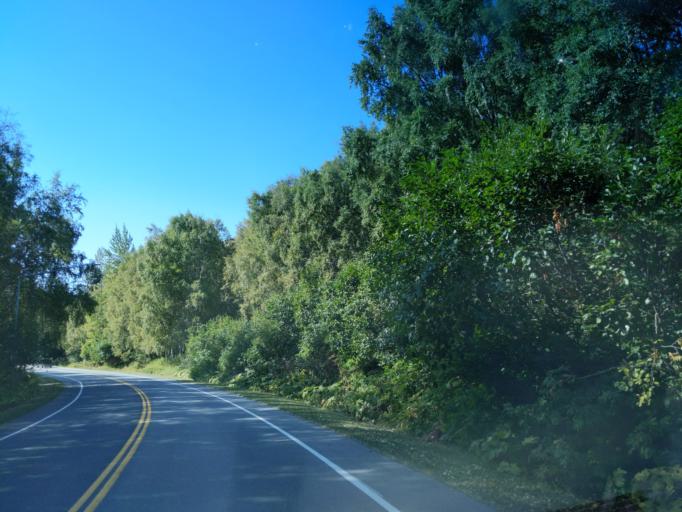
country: US
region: Alaska
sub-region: Anchorage Municipality
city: Anchorage
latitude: 61.1589
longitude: -150.0139
